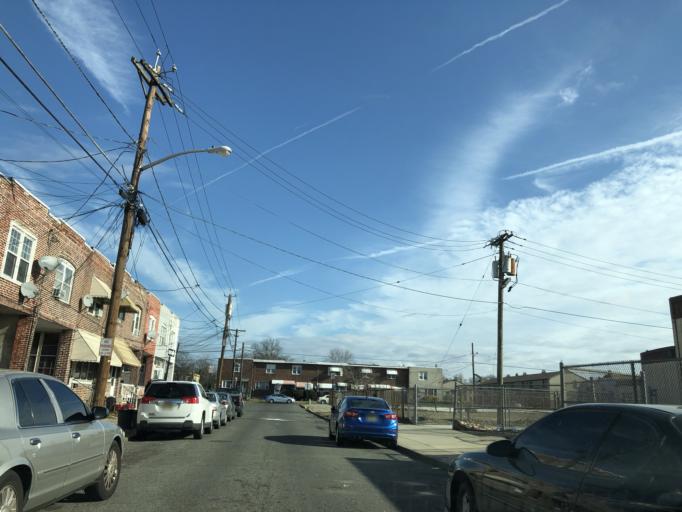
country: US
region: New Jersey
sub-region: Camden County
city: Camden
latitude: 39.9248
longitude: -75.1118
